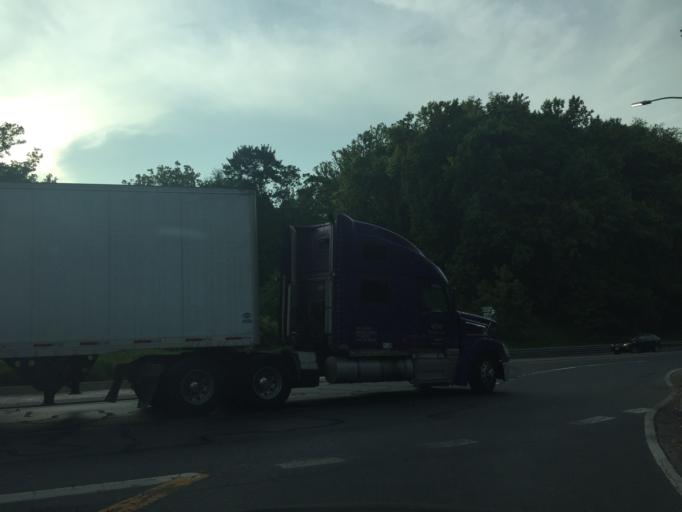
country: US
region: Maryland
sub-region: Frederick County
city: Point of Rocks
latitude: 39.2864
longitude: -77.5306
